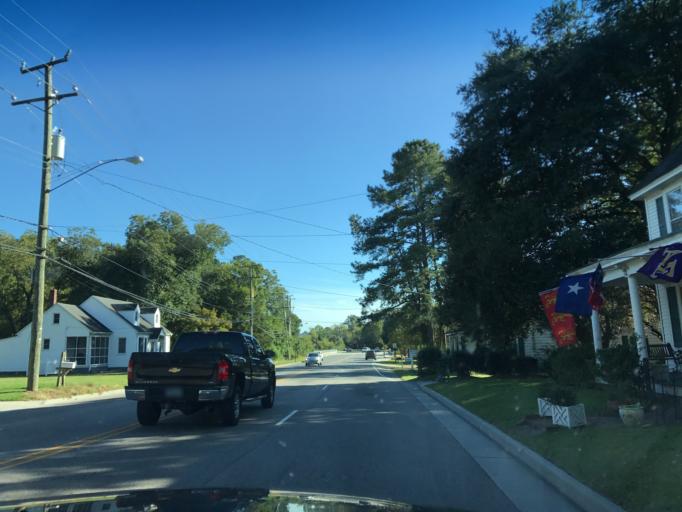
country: US
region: Virginia
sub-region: City of Portsmouth
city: Portsmouth Heights
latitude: 36.7484
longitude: -76.3462
